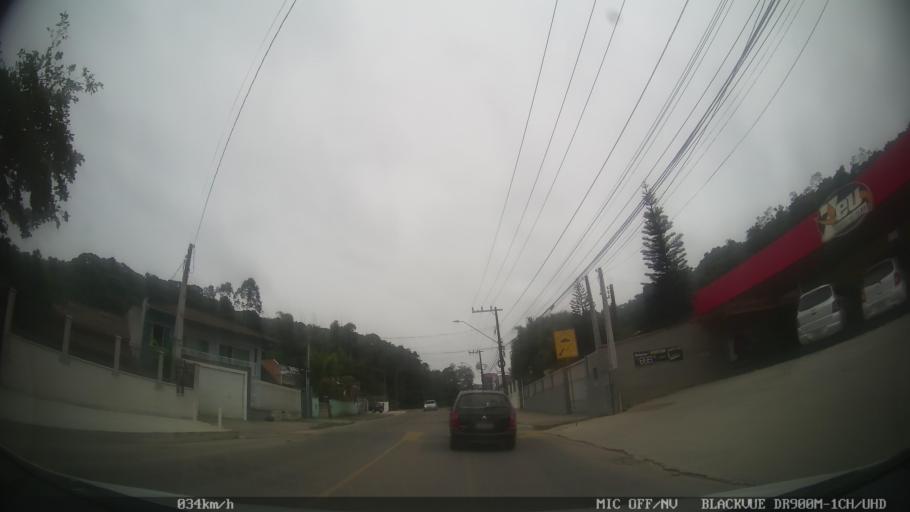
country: BR
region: Santa Catarina
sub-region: Joinville
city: Joinville
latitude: -26.3627
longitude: -48.8219
